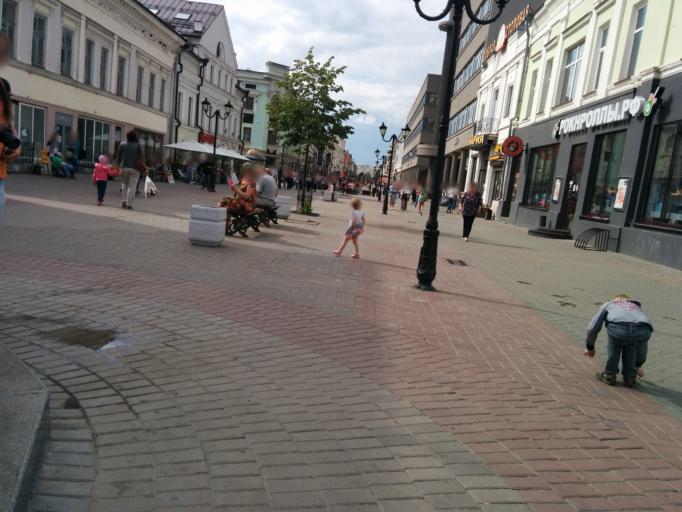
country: RU
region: Tatarstan
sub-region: Gorod Kazan'
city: Kazan
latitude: 55.7904
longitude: 49.1155
